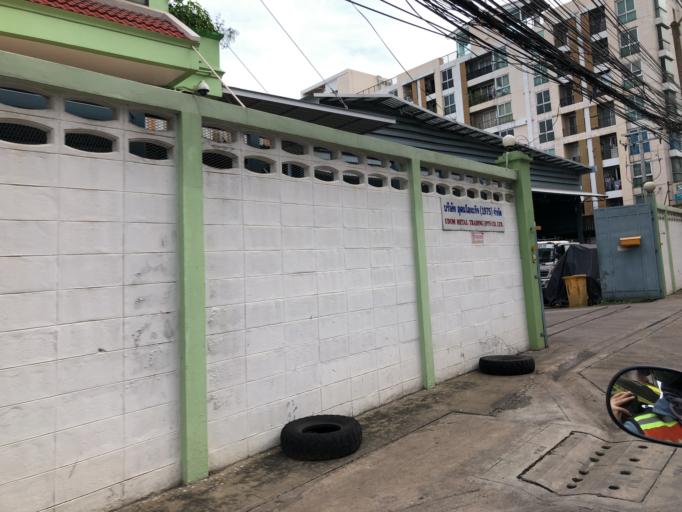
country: TH
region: Bangkok
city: Yan Nawa
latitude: 13.7102
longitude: 100.5481
